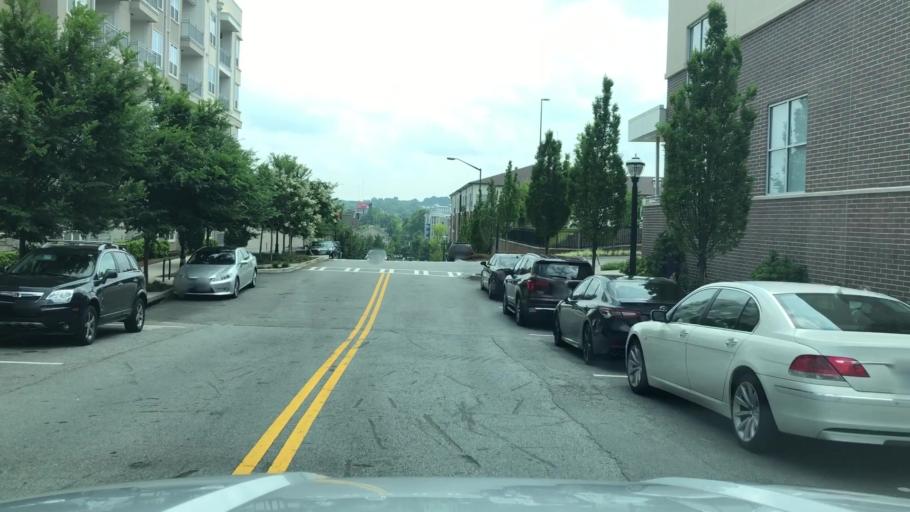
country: US
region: Georgia
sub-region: DeKalb County
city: North Atlanta
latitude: 33.8228
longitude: -84.3651
